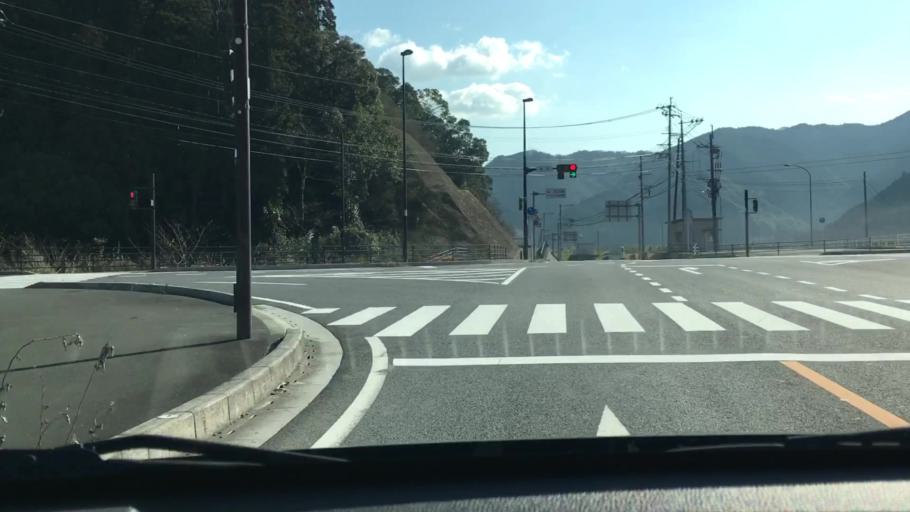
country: JP
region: Oita
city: Saiki
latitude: 32.9578
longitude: 131.8454
